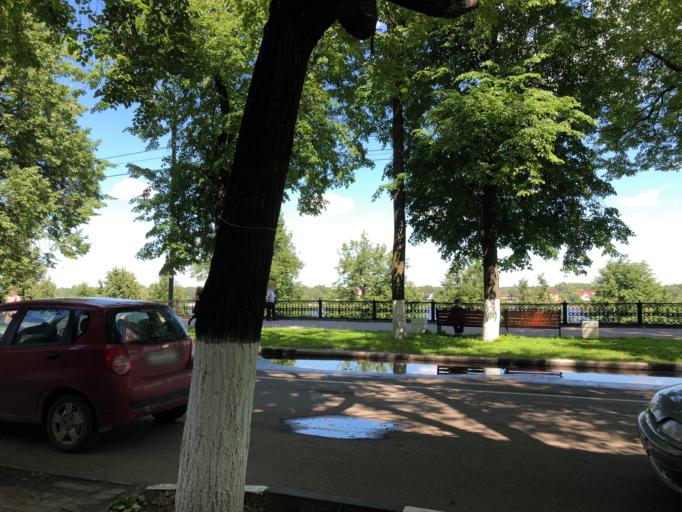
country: RU
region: Jaroslavl
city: Yaroslavl
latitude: 57.6311
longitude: 39.8946
